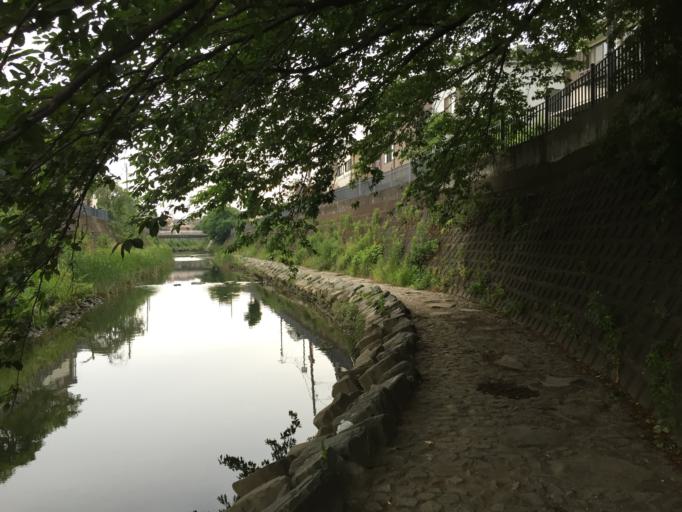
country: JP
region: Kanagawa
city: Yokohama
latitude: 35.4225
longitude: 139.5999
